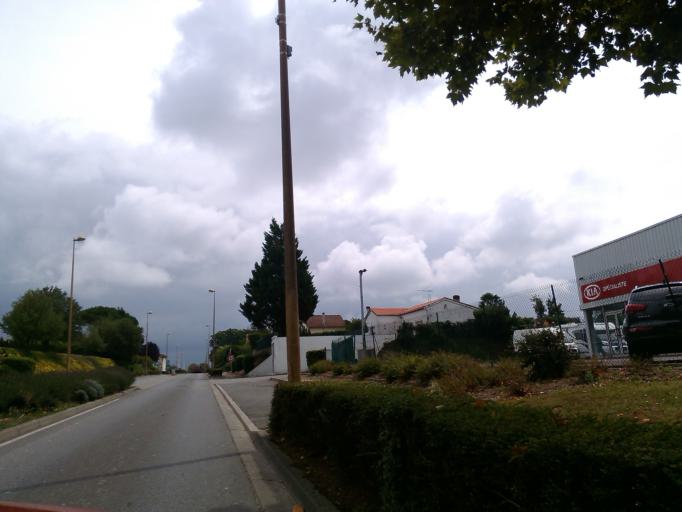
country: FR
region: Poitou-Charentes
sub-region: Departement de la Charente
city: Saint-Brice
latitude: 45.6851
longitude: -0.3036
